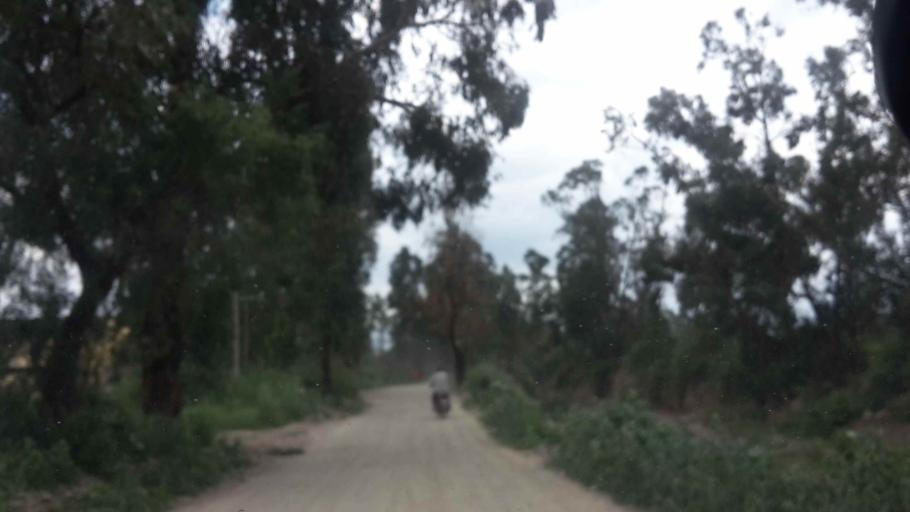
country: BO
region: Cochabamba
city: Cochabamba
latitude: -17.3331
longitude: -66.2242
